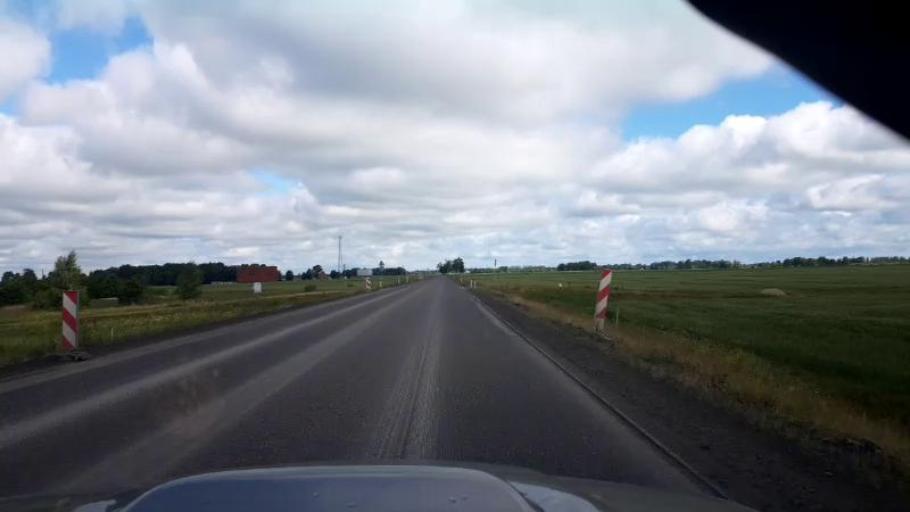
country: LV
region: Bauskas Rajons
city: Bauska
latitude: 56.2851
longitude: 24.3585
